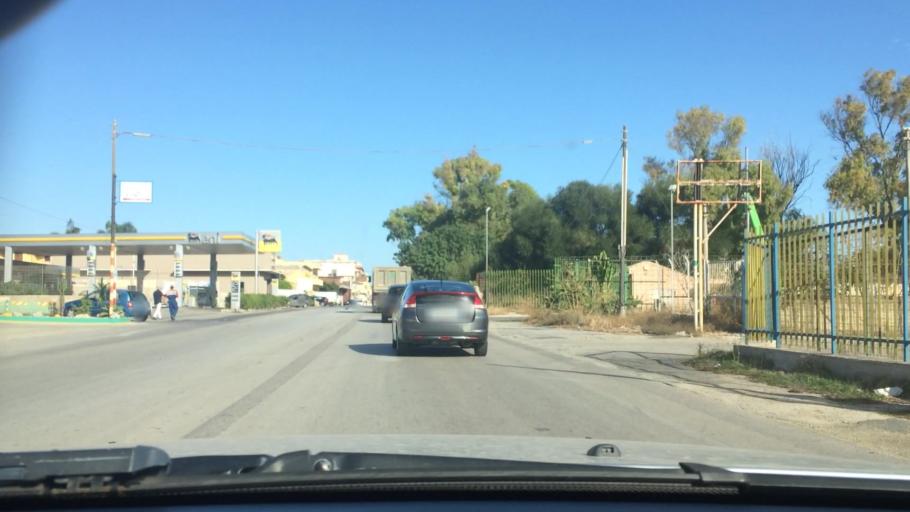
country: IT
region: Sicily
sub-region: Provincia di Siracusa
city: Priolo Gargallo
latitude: 37.1508
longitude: 15.1929
